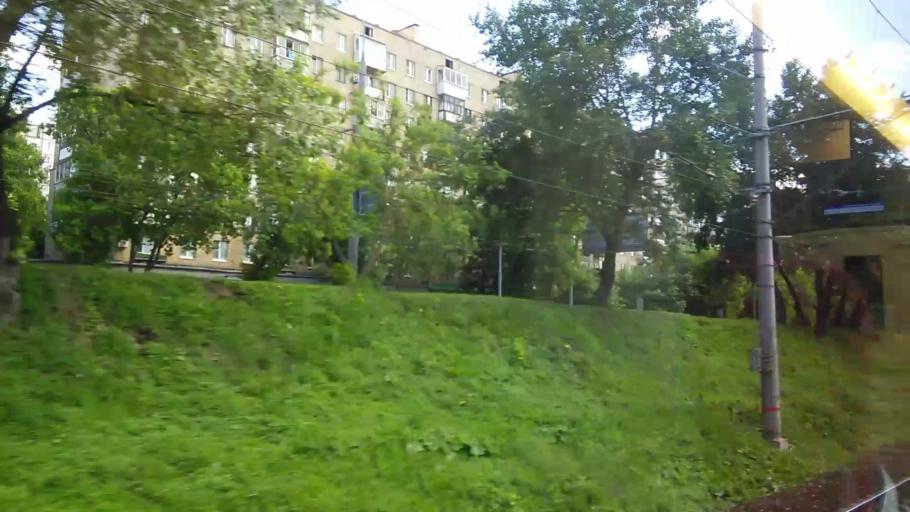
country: RU
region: Moscow
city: Mar'ina Roshcha
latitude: 55.7879
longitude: 37.5880
